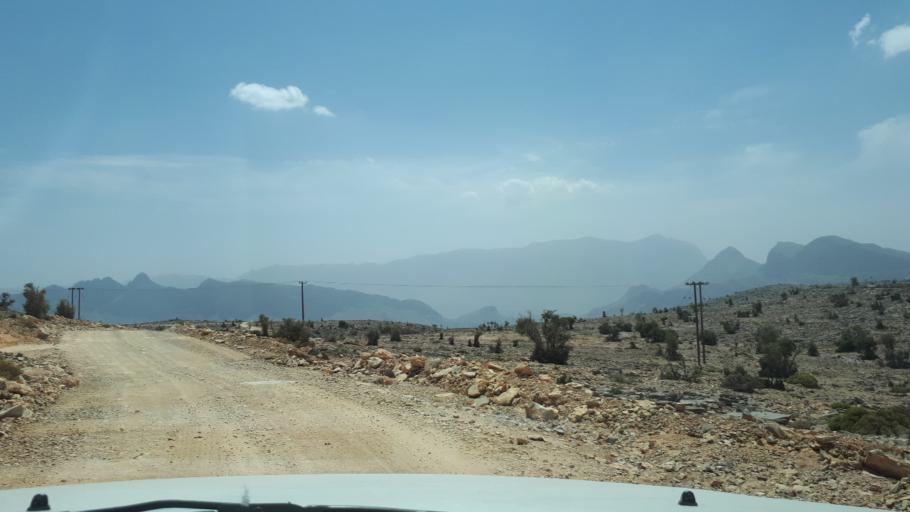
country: OM
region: Muhafazat ad Dakhiliyah
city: Bahla'
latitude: 23.1991
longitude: 57.2010
